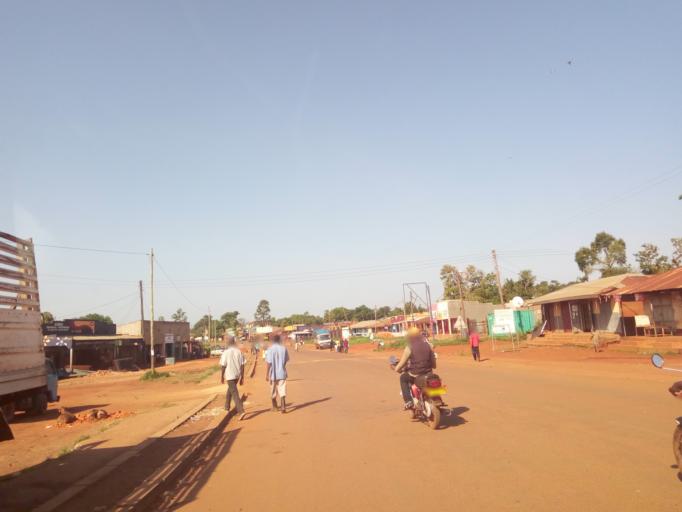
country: UG
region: Western Region
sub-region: Masindi District
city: Masindi
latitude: 1.6940
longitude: 31.7101
